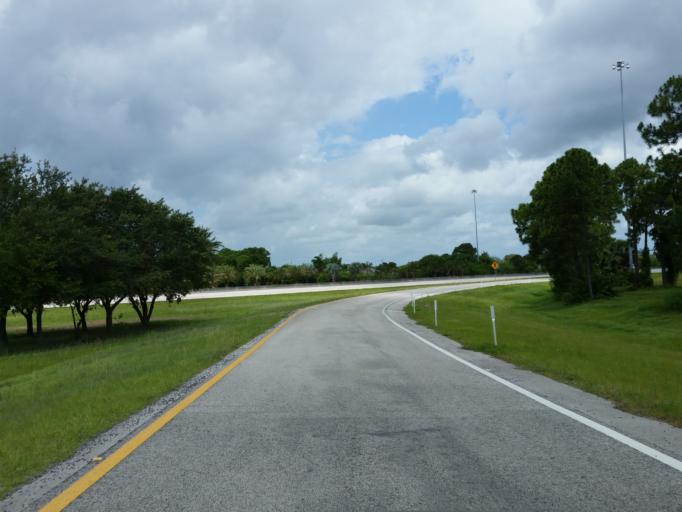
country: US
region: Florida
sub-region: Saint Lucie County
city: Port Saint Lucie
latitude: 27.2772
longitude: -80.3595
